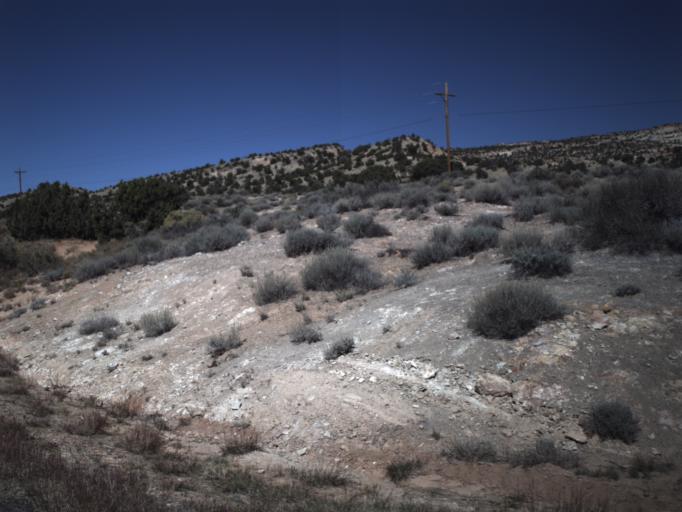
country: US
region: Utah
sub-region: Wayne County
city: Loa
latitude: 37.7462
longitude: -111.5627
